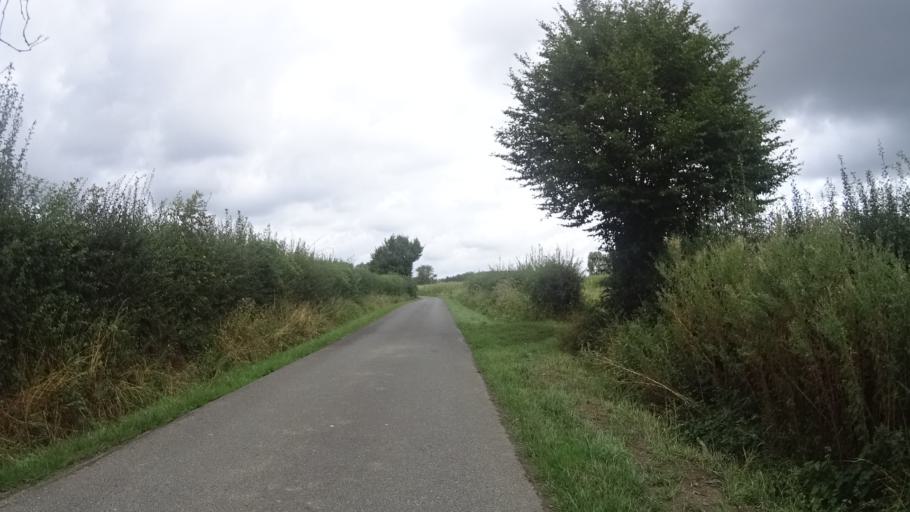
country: FR
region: Nord-Pas-de-Calais
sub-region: Departement du Nord
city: Maroilles
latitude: 50.1323
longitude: 3.7264
